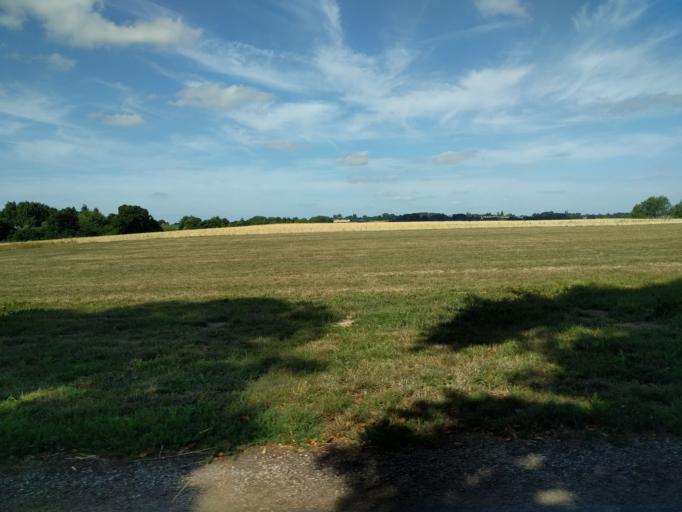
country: DK
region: Zealand
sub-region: Vordingborg Kommune
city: Stege
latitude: 54.9639
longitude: 12.2952
